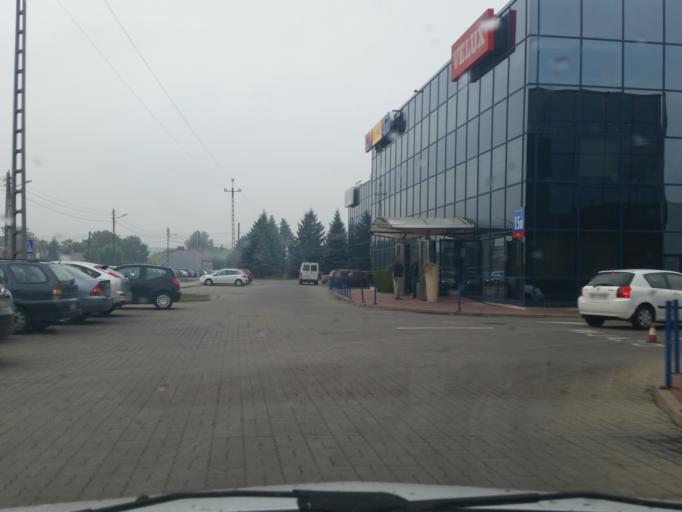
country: PL
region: Masovian Voivodeship
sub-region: Warszawa
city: Wlochy
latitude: 52.1785
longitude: 20.9378
